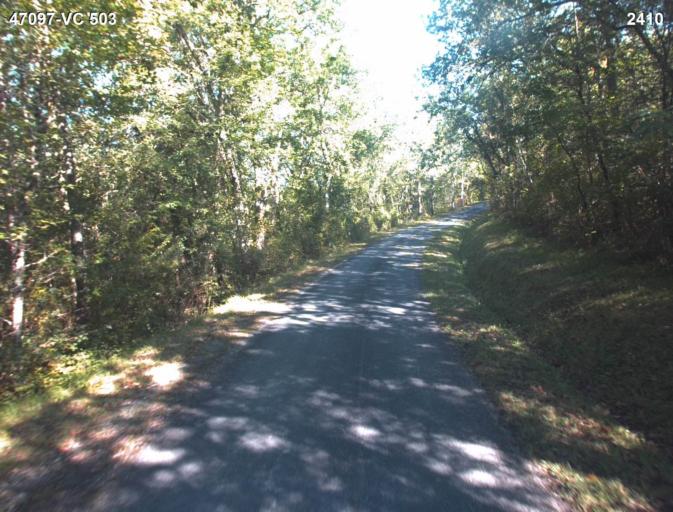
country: FR
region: Aquitaine
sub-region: Departement du Lot-et-Garonne
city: Port-Sainte-Marie
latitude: 44.2114
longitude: 0.3683
